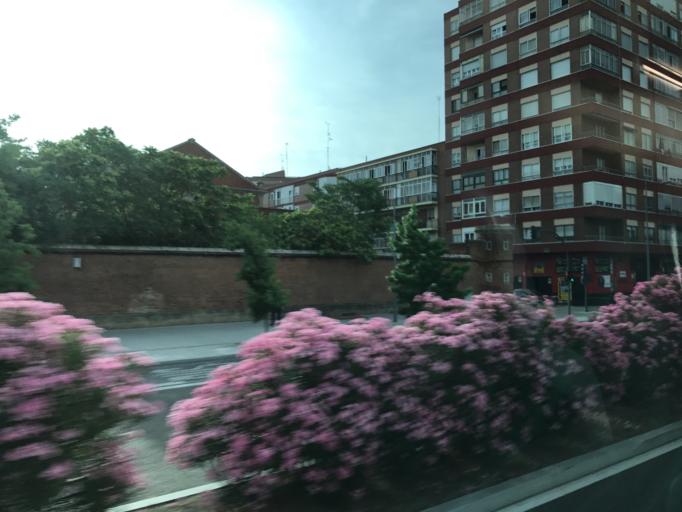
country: ES
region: Castille and Leon
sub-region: Provincia de Valladolid
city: Valladolid
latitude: 41.6316
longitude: -4.7282
